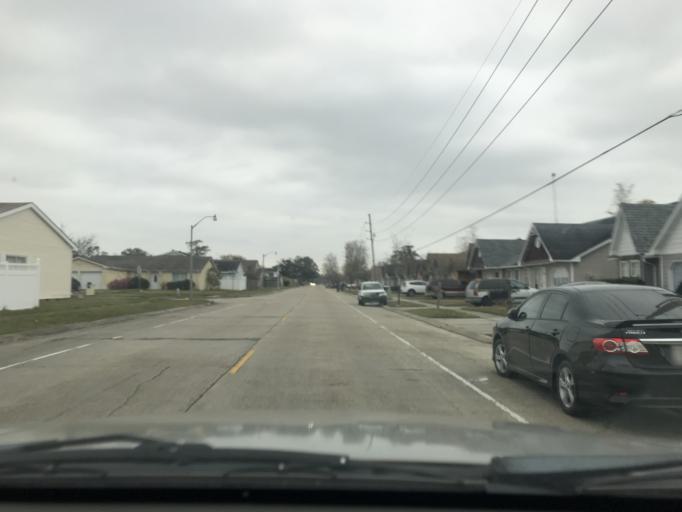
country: US
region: Louisiana
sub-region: Jefferson Parish
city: Woodmere
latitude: 29.8584
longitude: -90.0738
